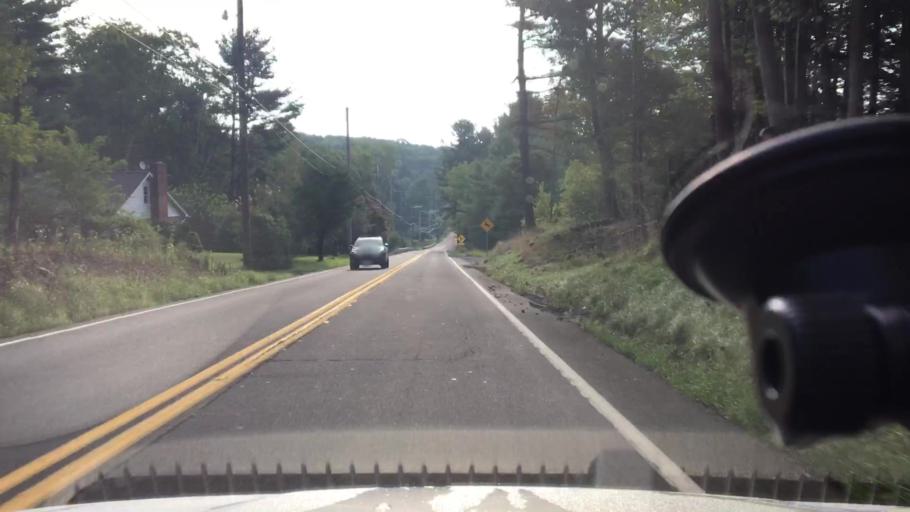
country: US
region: Pennsylvania
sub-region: Monroe County
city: Mount Pocono
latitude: 41.0993
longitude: -75.3393
